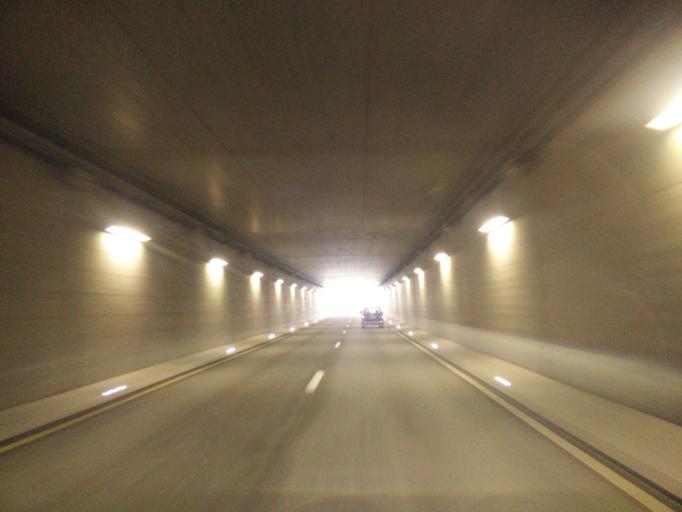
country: NO
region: Nord-Trondelag
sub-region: Stjordal
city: Stjordal
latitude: 63.4710
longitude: 10.9079
